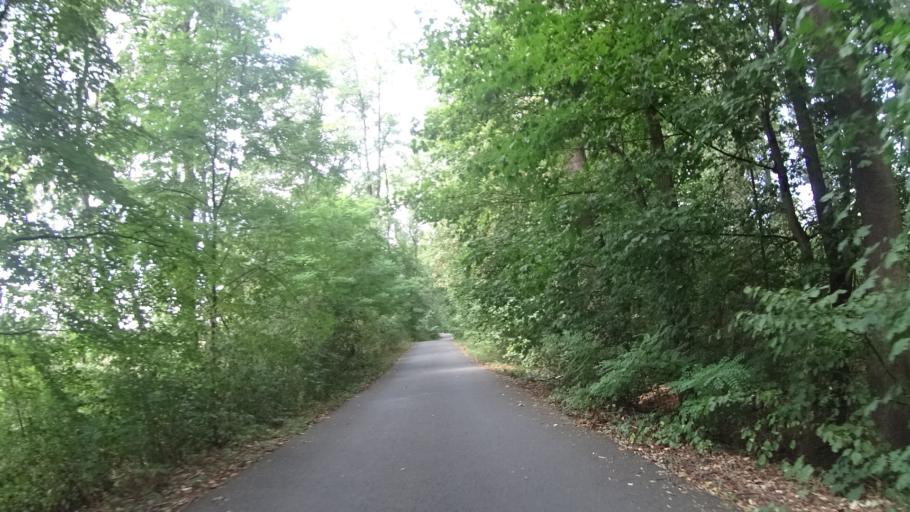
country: CZ
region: Olomoucky
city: Horka nad Moravou
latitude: 49.6489
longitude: 17.1959
